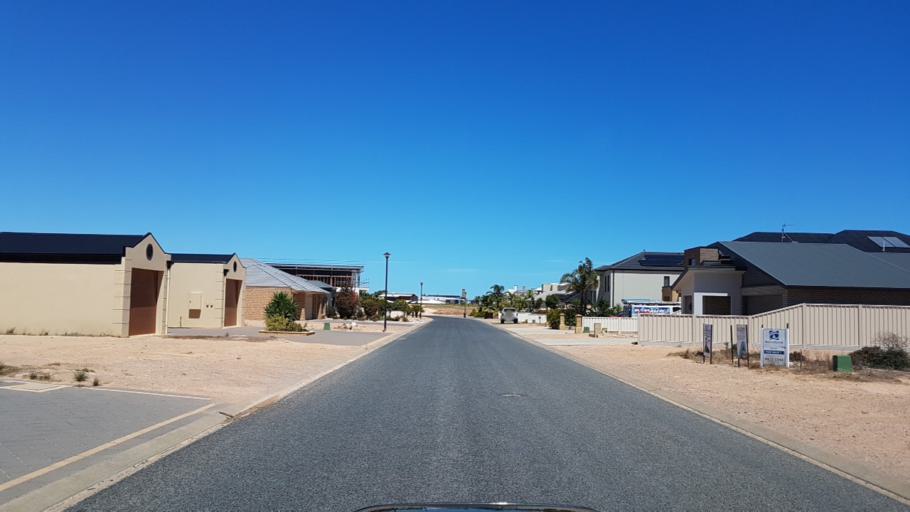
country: AU
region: South Australia
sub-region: Copper Coast
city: Wallaroo
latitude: -33.9187
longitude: 137.6397
